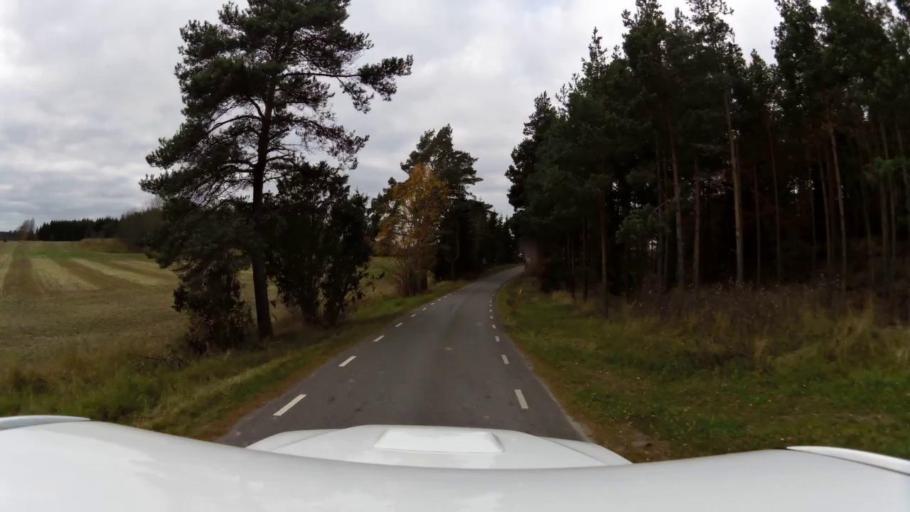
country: SE
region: OEstergoetland
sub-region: Linkopings Kommun
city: Linghem
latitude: 58.3920
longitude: 15.8039
